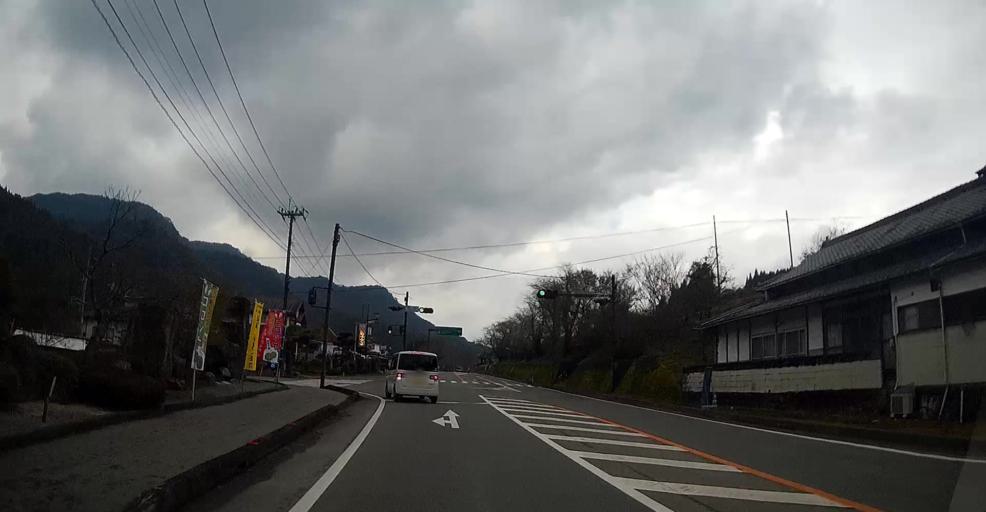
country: JP
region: Kumamoto
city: Matsubase
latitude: 32.6222
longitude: 130.8246
